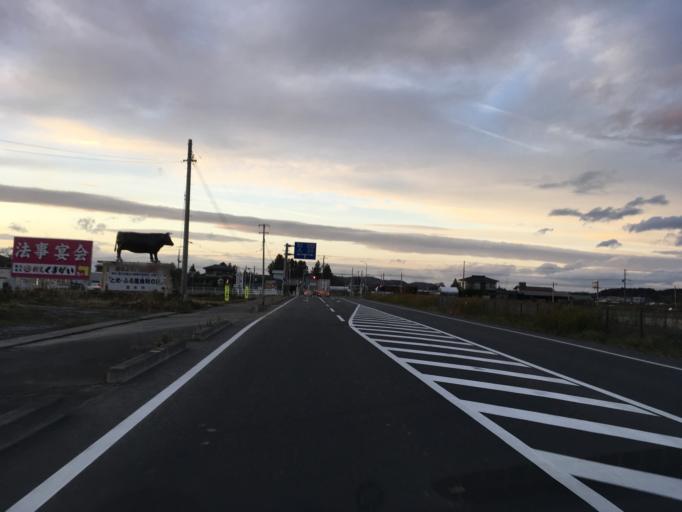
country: JP
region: Miyagi
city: Wakuya
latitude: 38.7189
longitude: 141.2560
